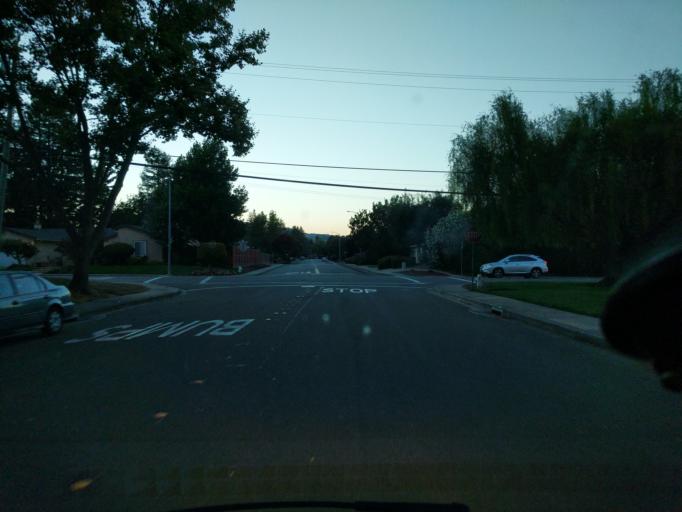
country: US
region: California
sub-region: Contra Costa County
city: San Ramon
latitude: 37.7671
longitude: -121.9794
